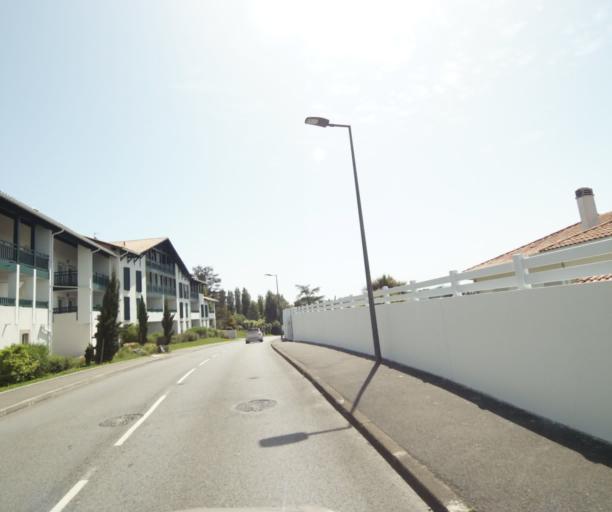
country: FR
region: Aquitaine
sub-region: Departement des Pyrenees-Atlantiques
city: Mouguerre
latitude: 43.4725
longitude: -1.4501
